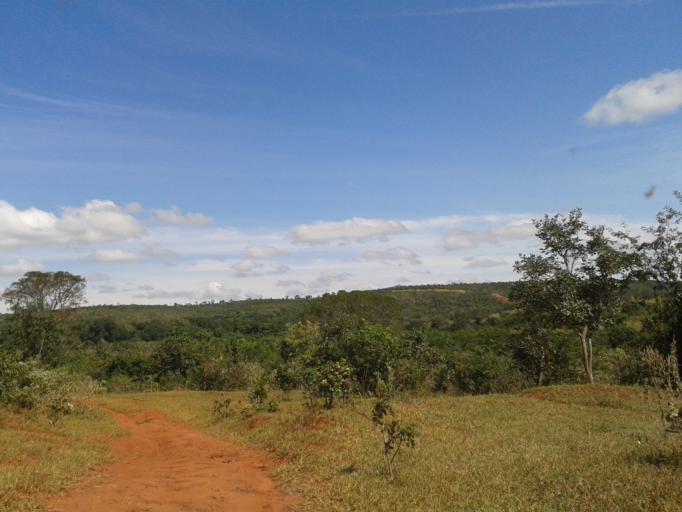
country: BR
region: Minas Gerais
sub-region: Campina Verde
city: Campina Verde
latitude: -19.4364
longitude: -49.7040
